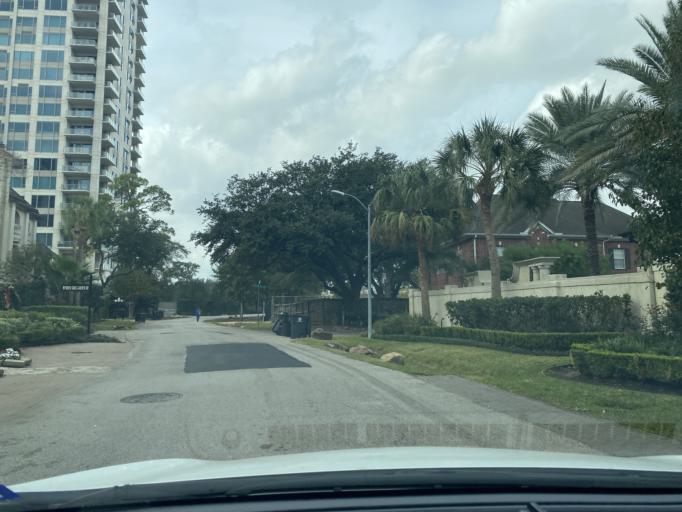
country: US
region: Texas
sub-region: Harris County
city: Hunters Creek Village
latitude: 29.7552
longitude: -95.4613
